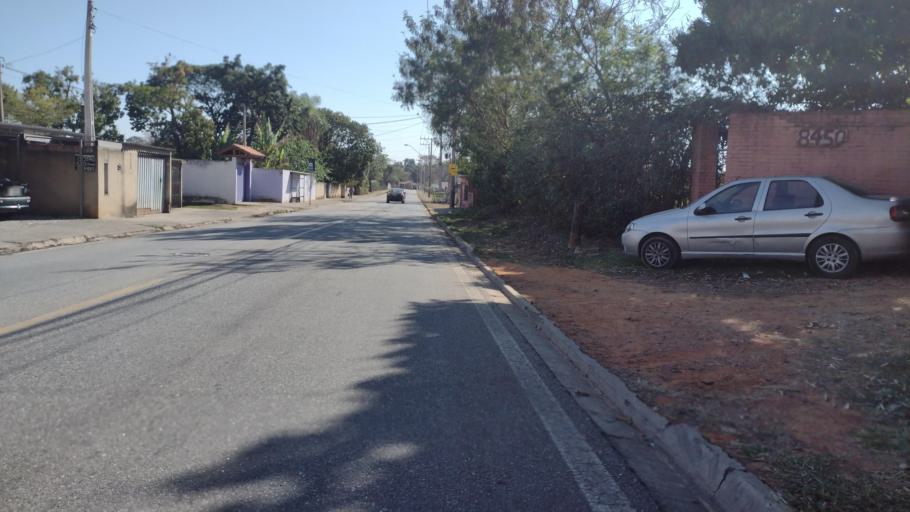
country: BR
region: Sao Paulo
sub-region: Sorocaba
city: Sorocaba
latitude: -23.4144
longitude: -47.4791
